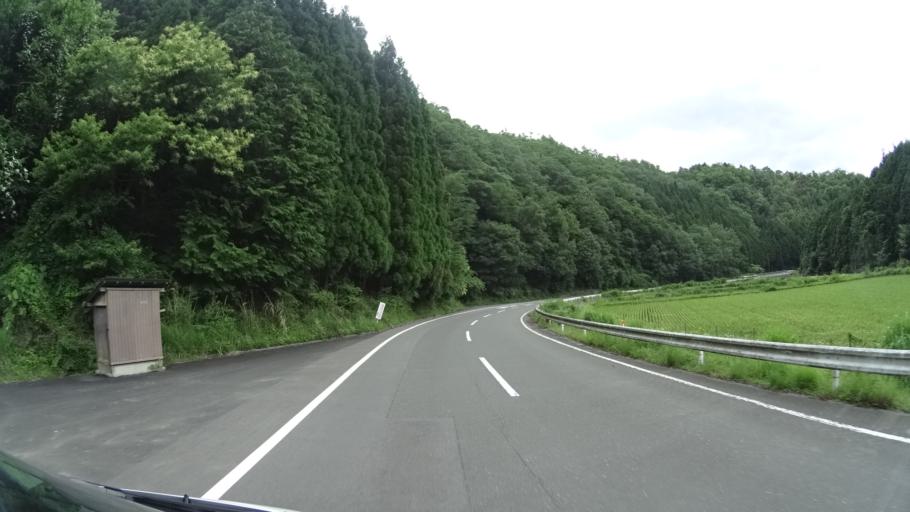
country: JP
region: Hyogo
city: Sasayama
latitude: 35.0635
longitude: 135.3917
